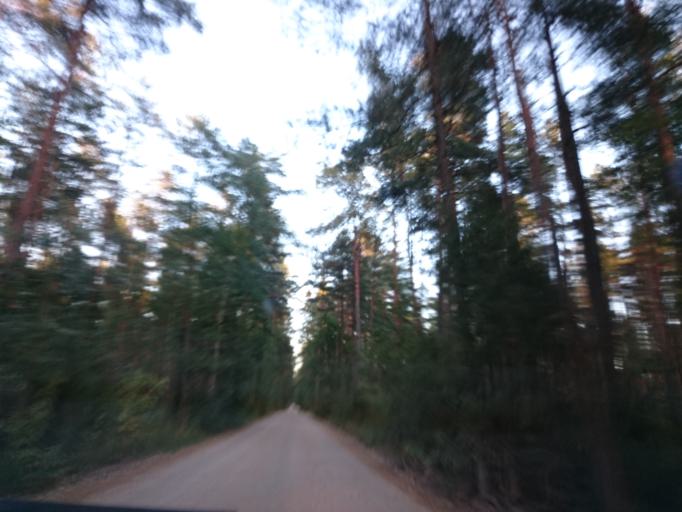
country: LV
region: Adazi
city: Adazi
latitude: 57.0530
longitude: 24.3064
